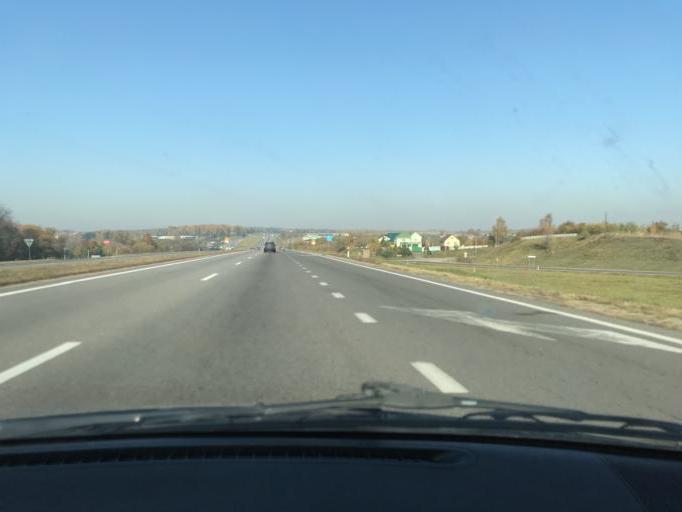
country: BY
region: Minsk
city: Samakhvalavichy
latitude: 53.7367
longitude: 27.5161
